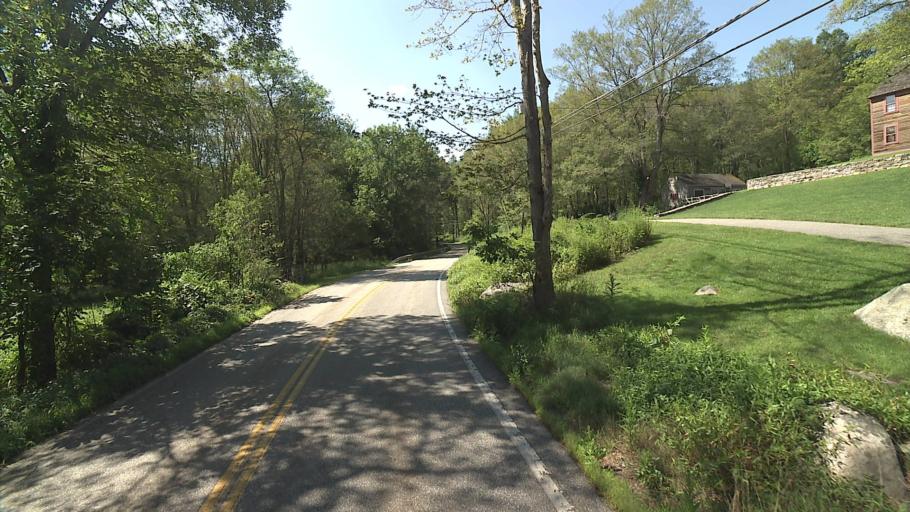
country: US
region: Connecticut
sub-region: Tolland County
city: Mansfield City
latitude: 41.8088
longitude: -72.1701
